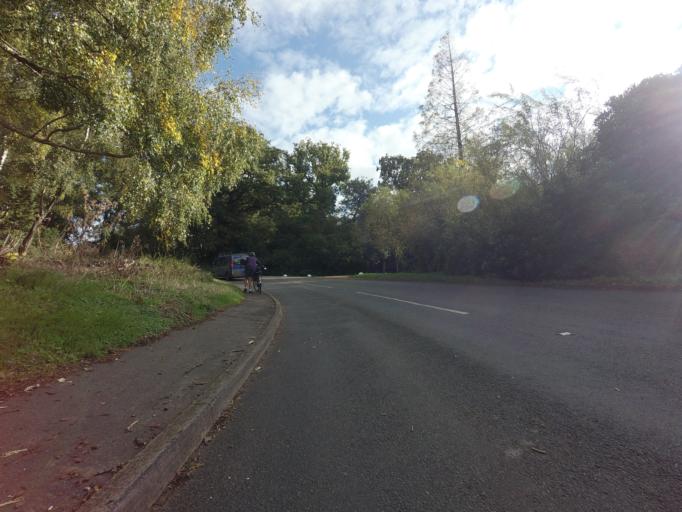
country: GB
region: England
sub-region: Norfolk
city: Dersingham
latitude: 52.8374
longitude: 0.5087
